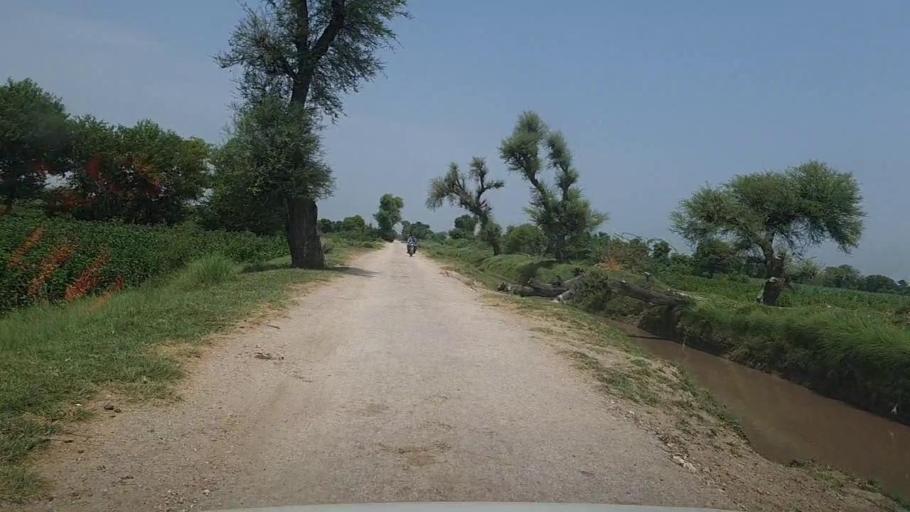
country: PK
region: Sindh
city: Karaundi
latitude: 26.8902
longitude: 68.3332
